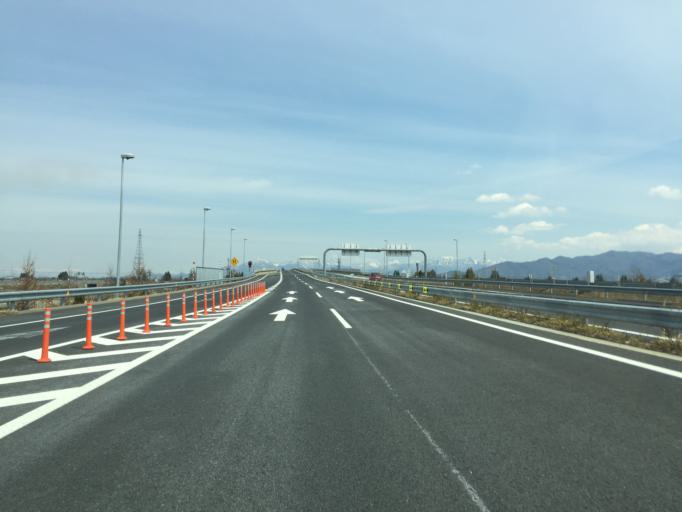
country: JP
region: Yamagata
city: Tendo
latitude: 38.3065
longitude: 140.3144
